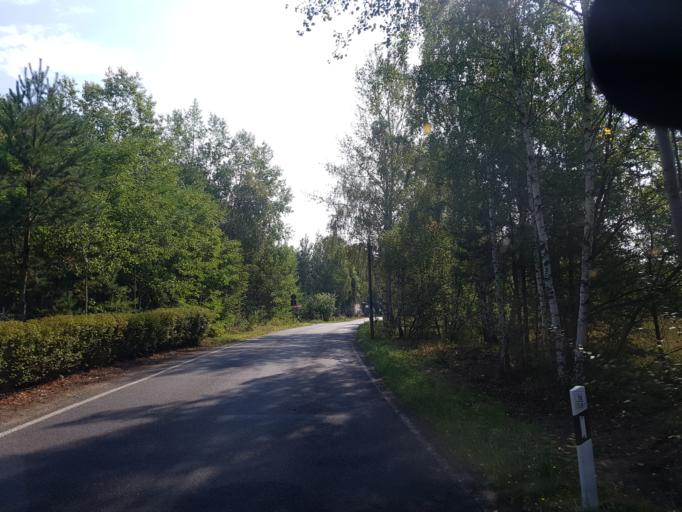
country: DE
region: Brandenburg
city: Lauchhammer
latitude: 51.5115
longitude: 13.7275
